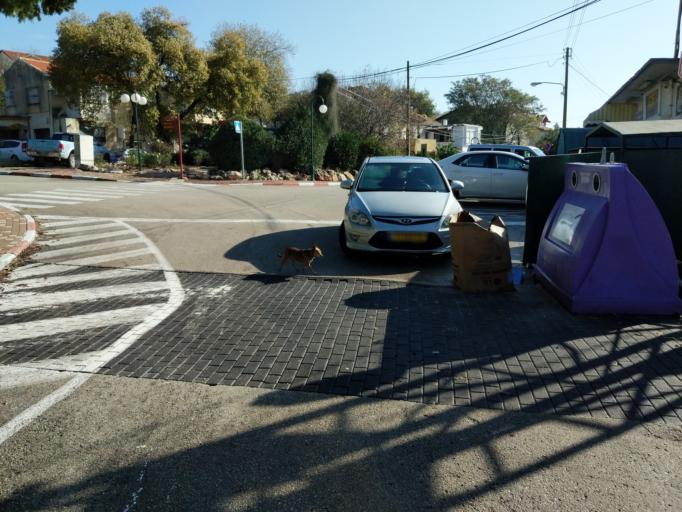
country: IL
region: Northern District
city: Basmat Tab`un
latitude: 32.7259
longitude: 35.1400
